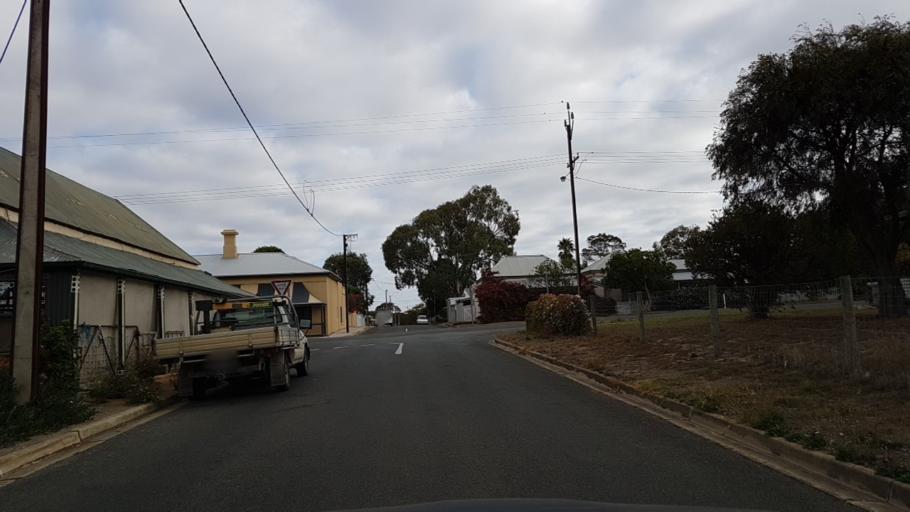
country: AU
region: South Australia
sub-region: Alexandrina
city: Langhorne Creek
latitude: -35.4065
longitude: 138.9717
